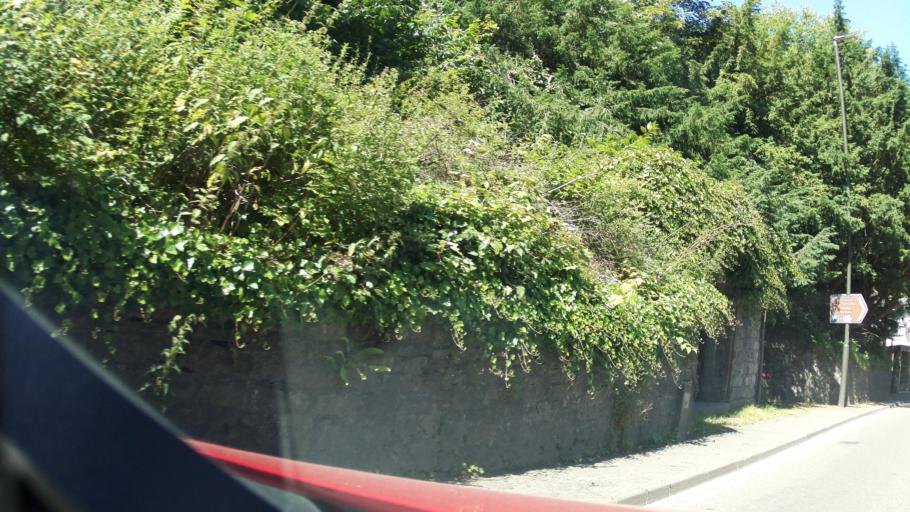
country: GB
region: England
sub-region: Derbyshire
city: Cromford
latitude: 53.1190
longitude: -1.5626
